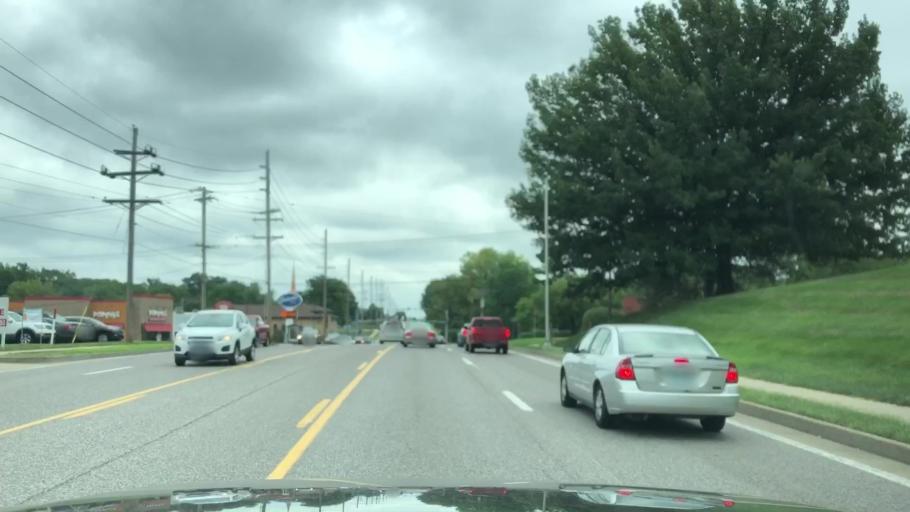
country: US
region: Missouri
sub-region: Saint Louis County
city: Florissant
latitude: 38.7997
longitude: -90.3305
